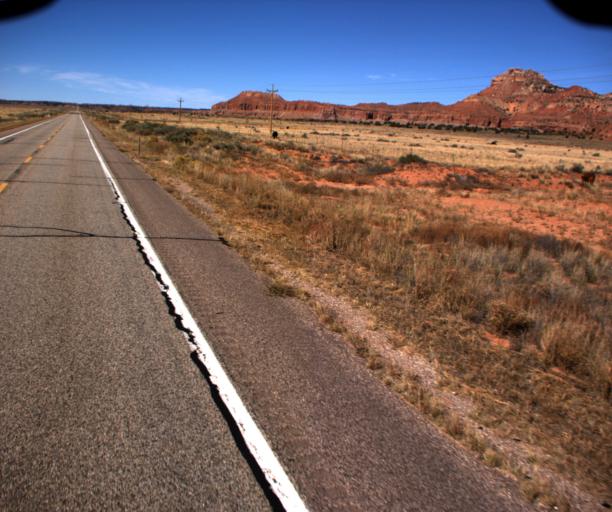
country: US
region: Arizona
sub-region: Mohave County
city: Colorado City
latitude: 36.8643
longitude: -112.8314
